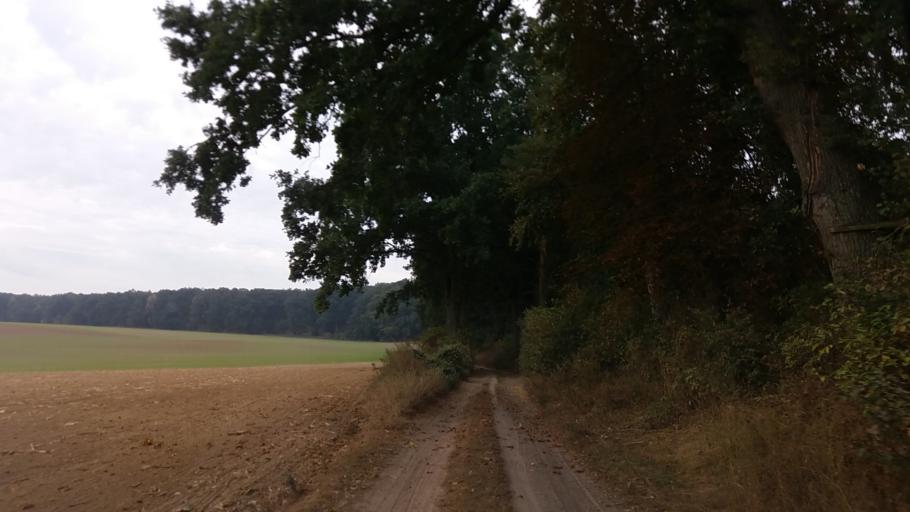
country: PL
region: West Pomeranian Voivodeship
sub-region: Powiat choszczenski
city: Pelczyce
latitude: 53.0792
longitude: 15.2940
